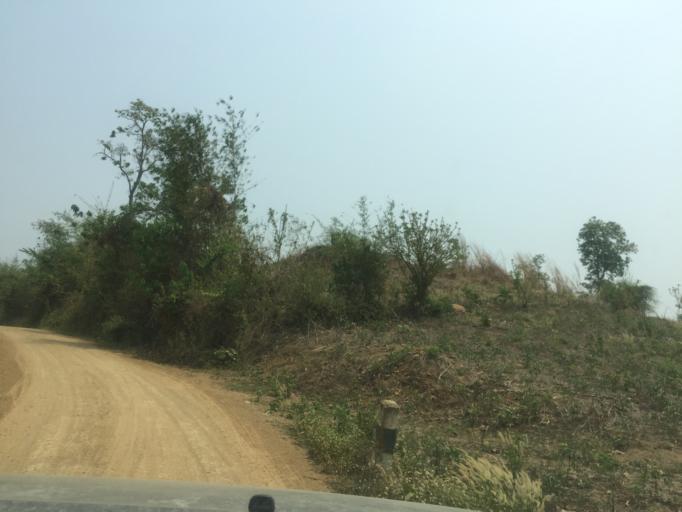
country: LA
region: Xiagnabouli
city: Muang Kenthao
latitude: 17.7869
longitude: 101.2529
